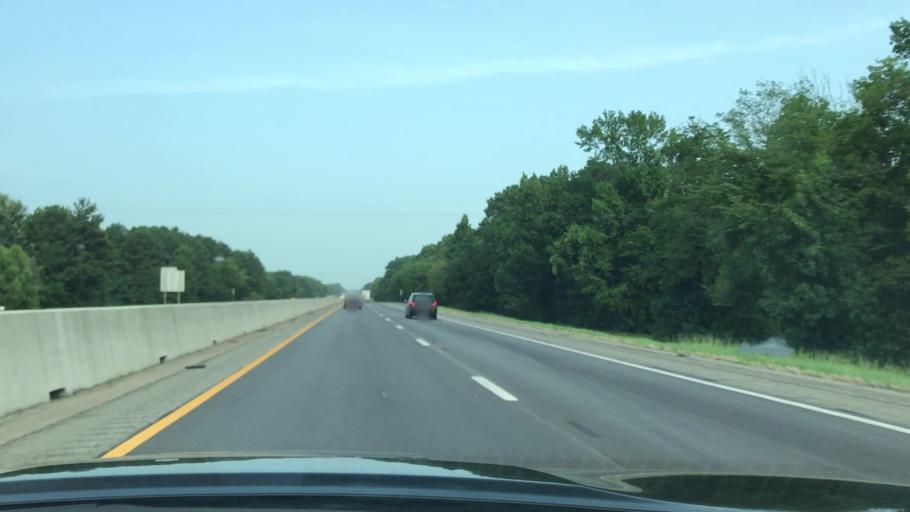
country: US
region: Texas
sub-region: Gregg County
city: Kilgore
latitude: 32.4326
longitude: -94.8806
